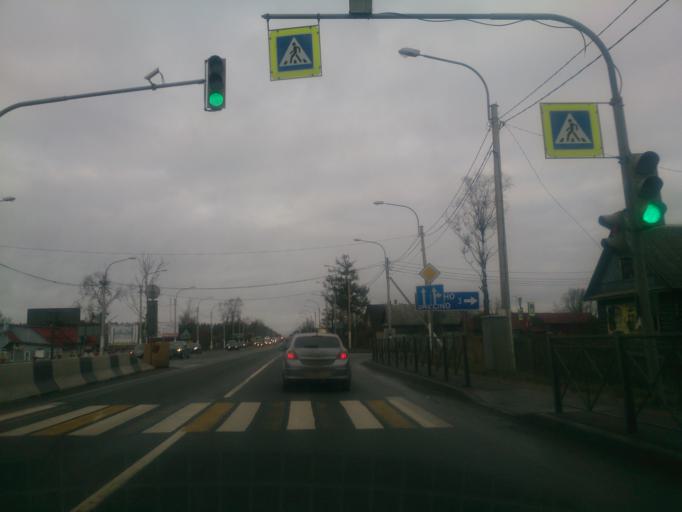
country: RU
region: Leningrad
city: Ul'yanovka
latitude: 59.6172
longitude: 30.7384
